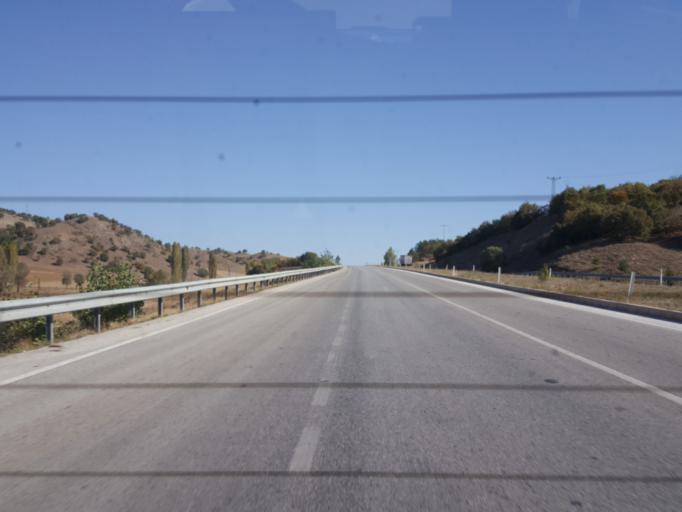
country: TR
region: Corum
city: Alaca
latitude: 40.2764
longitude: 34.6424
